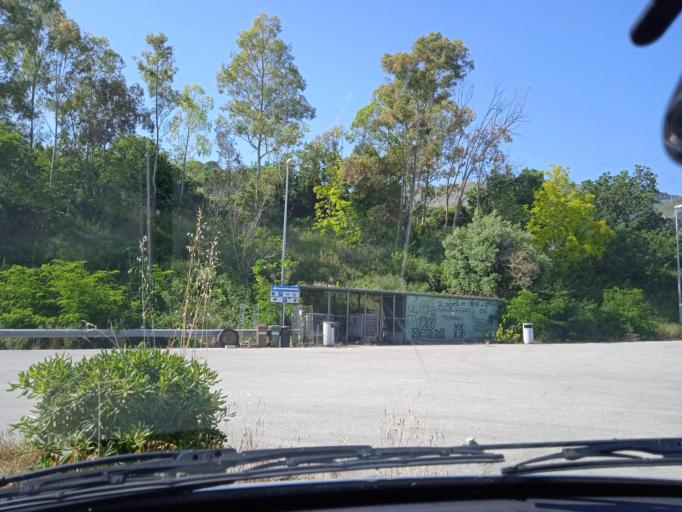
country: IT
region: Sicily
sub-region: Messina
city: Acquedolci
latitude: 38.0534
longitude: 14.6020
